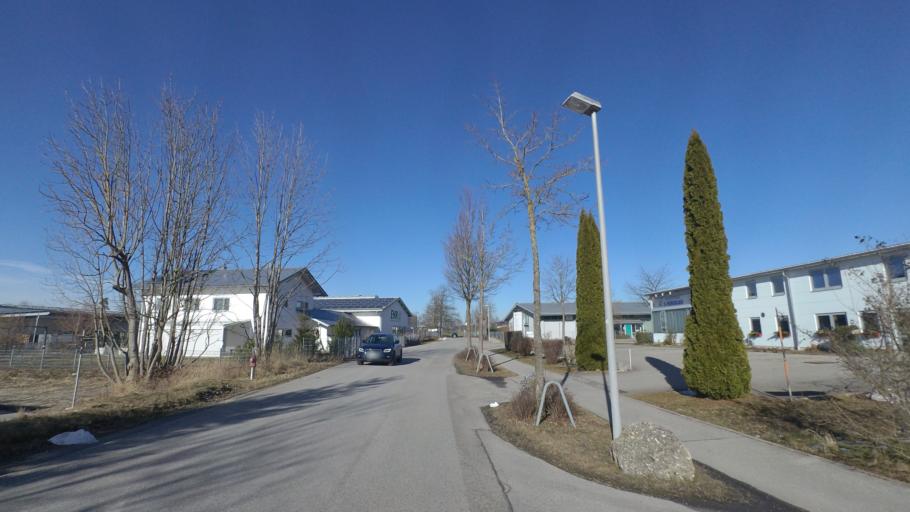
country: DE
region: Bavaria
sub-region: Upper Bavaria
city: Traunreut
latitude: 47.9621
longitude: 12.6124
